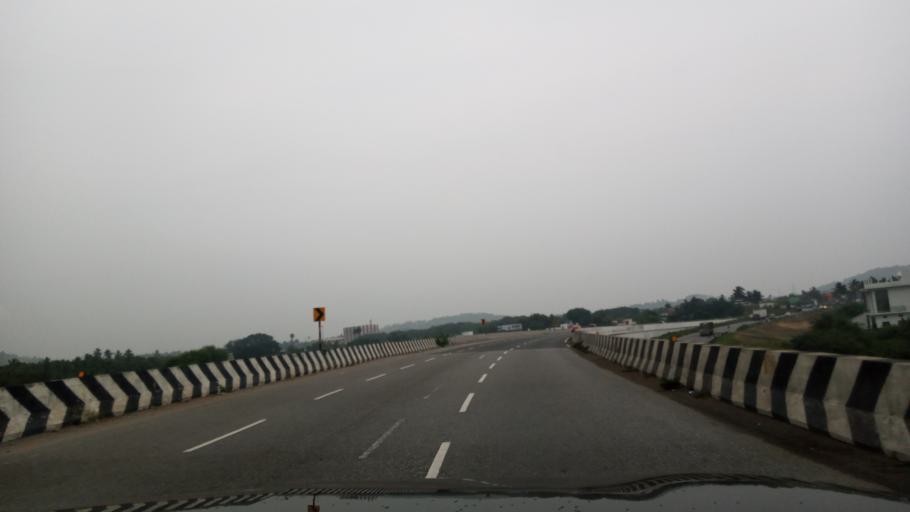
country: IN
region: Tamil Nadu
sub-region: Vellore
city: Walajapet
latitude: 12.9168
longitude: 79.3864
